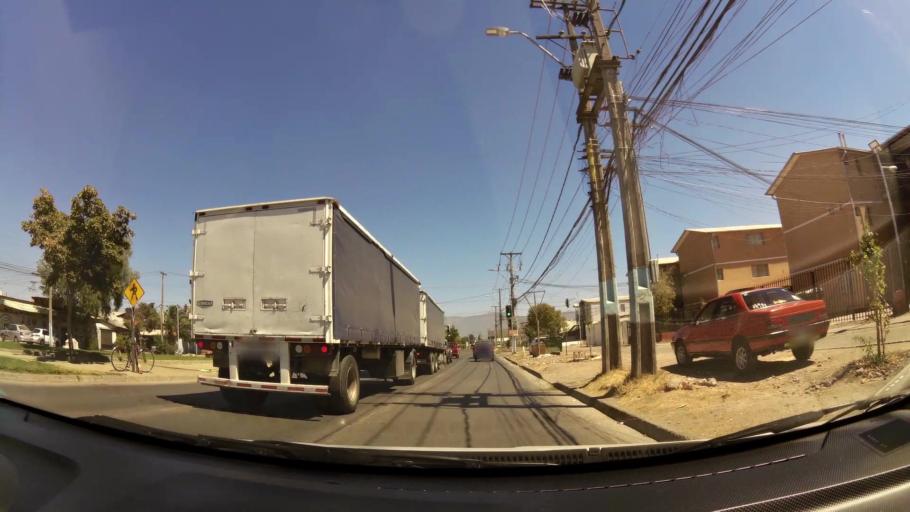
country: CL
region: O'Higgins
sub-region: Provincia de Cachapoal
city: Rancagua
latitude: -34.1568
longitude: -70.7249
